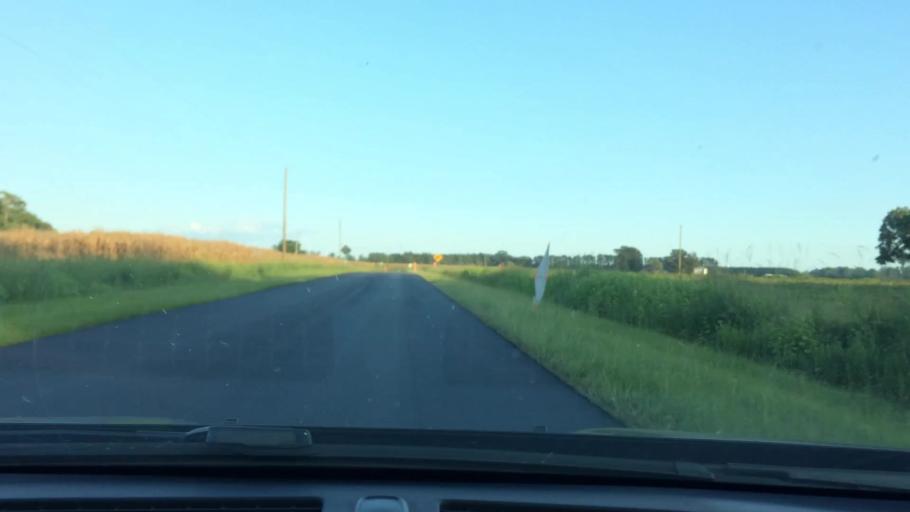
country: US
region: North Carolina
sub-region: Pitt County
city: Ayden
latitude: 35.4445
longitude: -77.4567
